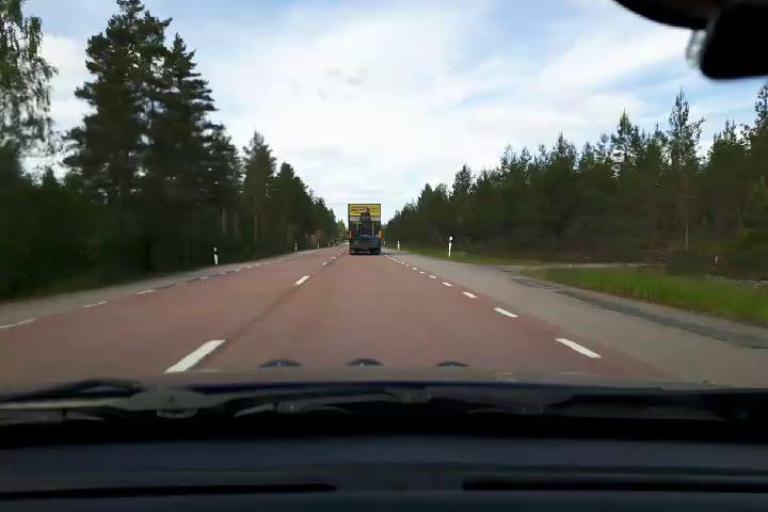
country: SE
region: Uppsala
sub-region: Osthammars Kommun
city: Bjorklinge
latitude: 60.1721
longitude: 17.4875
